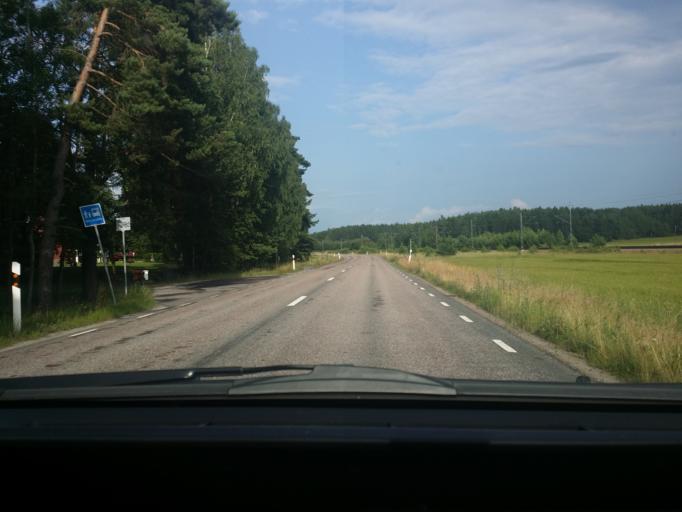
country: SE
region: Vaestmanland
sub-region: Hallstahammars Kommun
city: Kolback
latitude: 59.5662
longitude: 16.3598
